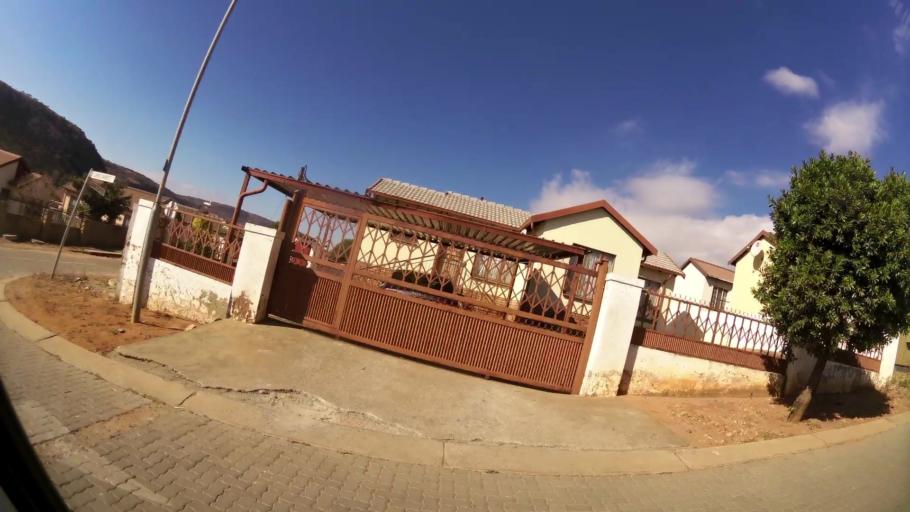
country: ZA
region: Gauteng
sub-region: City of Tshwane Metropolitan Municipality
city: Cullinan
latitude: -25.6915
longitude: 28.4168
